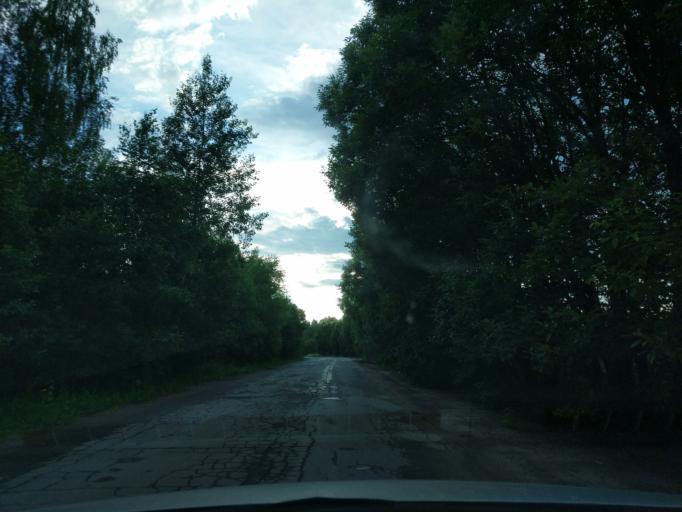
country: RU
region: Kaluga
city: Myatlevo
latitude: 54.8528
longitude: 35.5938
